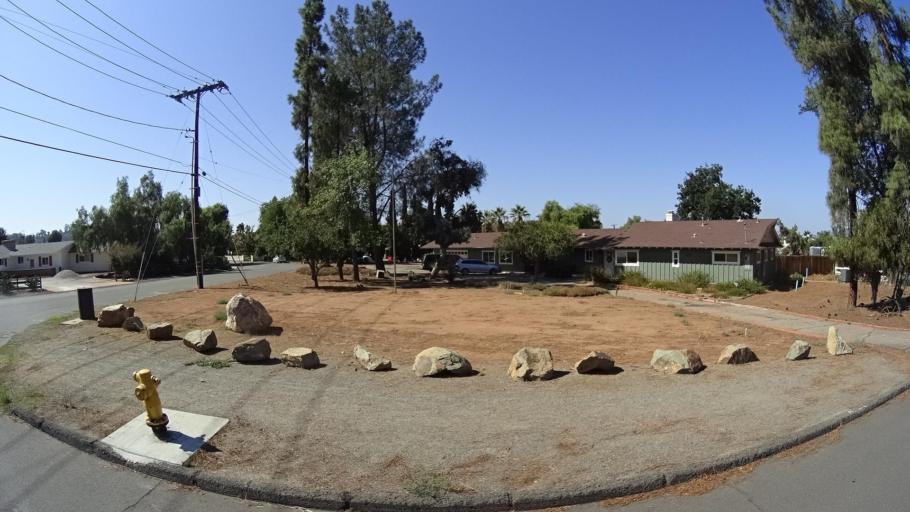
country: US
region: California
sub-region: San Diego County
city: Granite Hills
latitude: 32.7915
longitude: -116.9200
